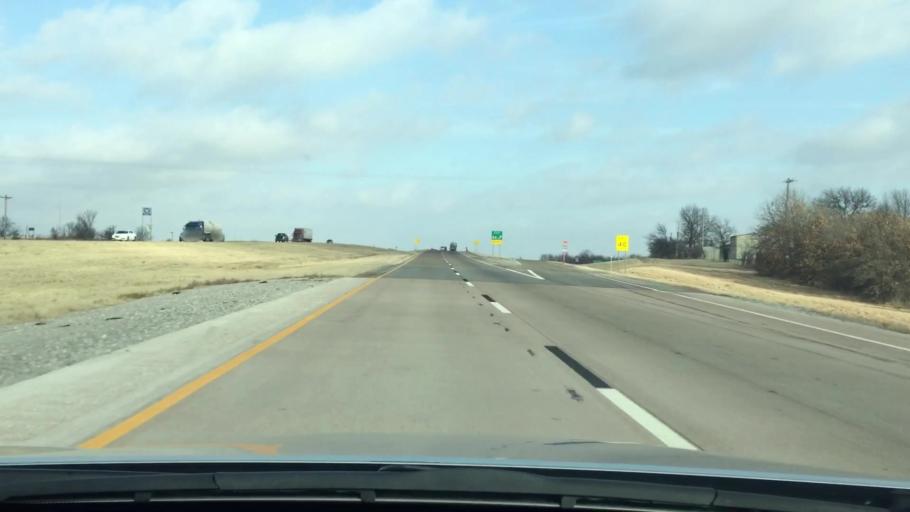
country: US
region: Oklahoma
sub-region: Garvin County
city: Wynnewood
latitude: 34.6474
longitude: -97.2198
